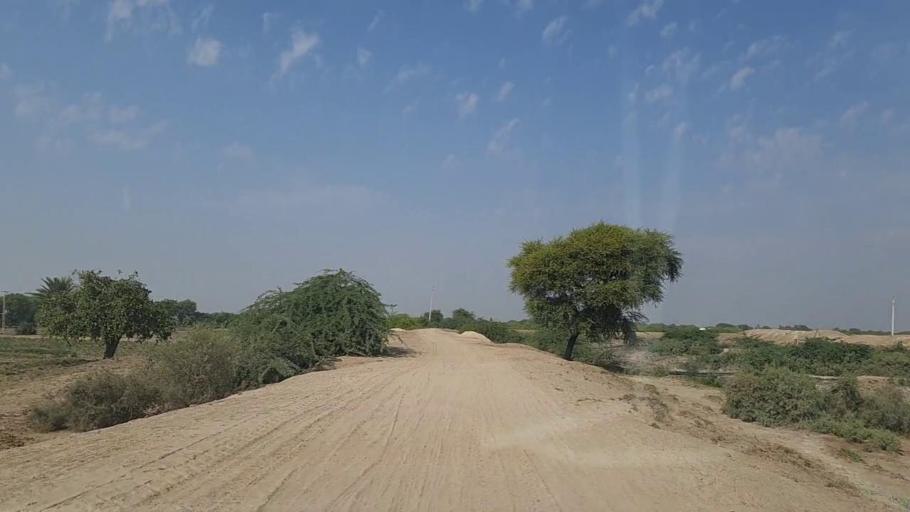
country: PK
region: Sindh
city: Mirpur Batoro
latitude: 24.6752
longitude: 68.3739
